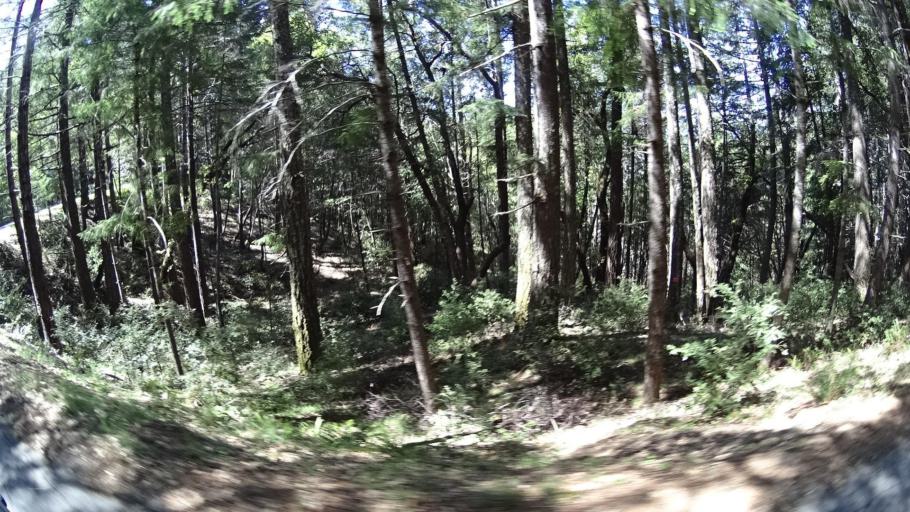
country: US
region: California
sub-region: Humboldt County
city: Redway
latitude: 40.0997
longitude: -123.9495
